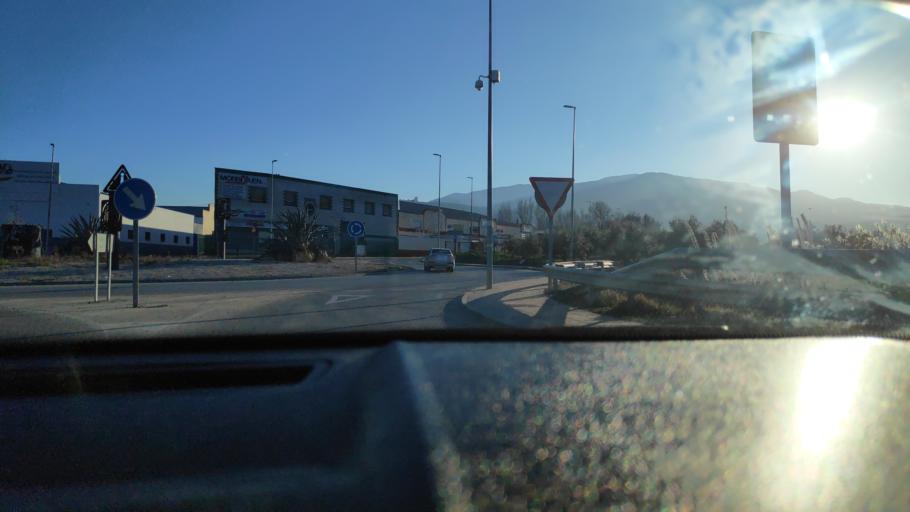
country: ES
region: Andalusia
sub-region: Provincia de Jaen
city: Jaen
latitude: 37.8027
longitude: -3.7882
